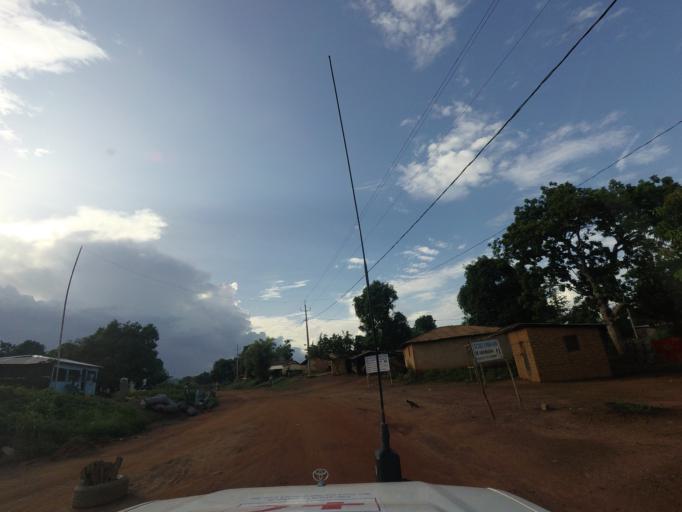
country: GN
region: Nzerekore
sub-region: Nzerekore Prefecture
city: Nzerekore
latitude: 7.7267
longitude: -8.8259
